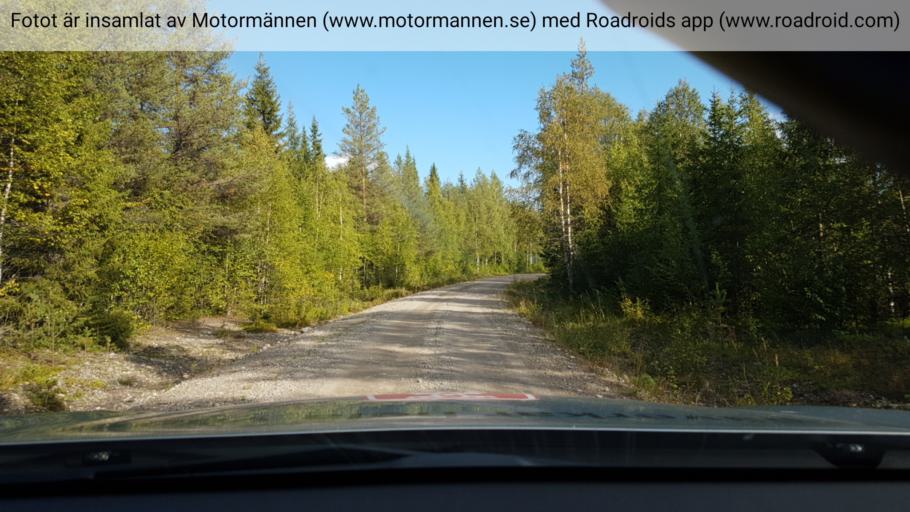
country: SE
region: Vaesterbotten
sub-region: Sorsele Kommun
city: Sorsele
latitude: 65.4702
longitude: 17.8591
